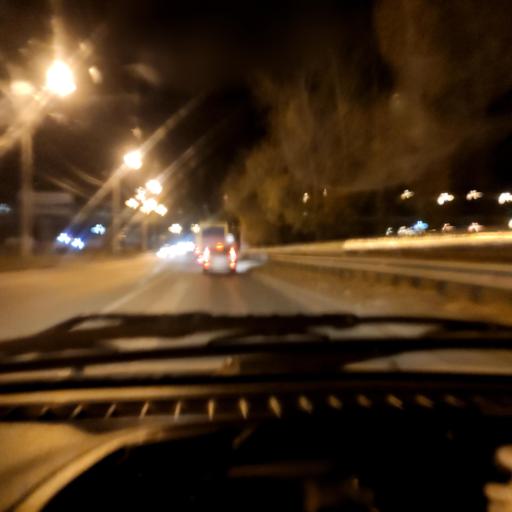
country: RU
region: Samara
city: Zhigulevsk
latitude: 53.4852
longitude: 49.5123
